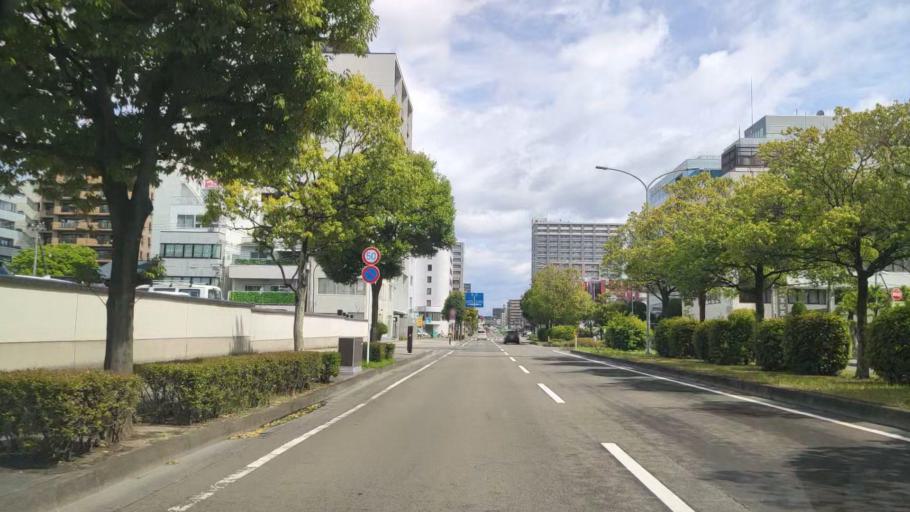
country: JP
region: Miyagi
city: Sendai-shi
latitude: 38.2576
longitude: 140.8913
